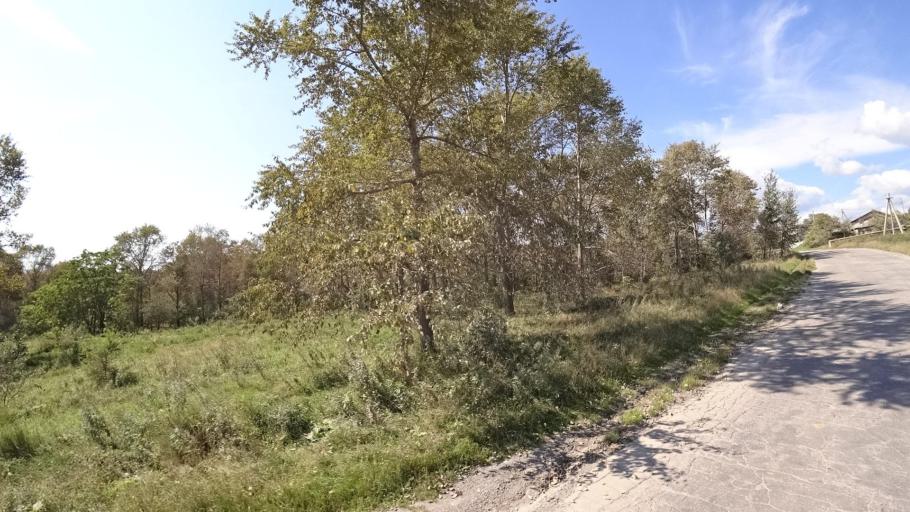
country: RU
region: Jewish Autonomous Oblast
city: Londoko
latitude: 49.0071
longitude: 131.8894
